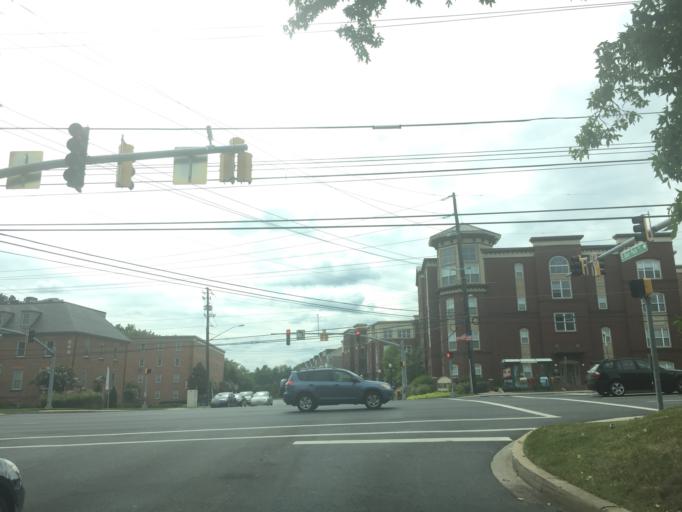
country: US
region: Maryland
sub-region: Montgomery County
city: Gaithersburg
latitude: 39.1324
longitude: -77.1885
